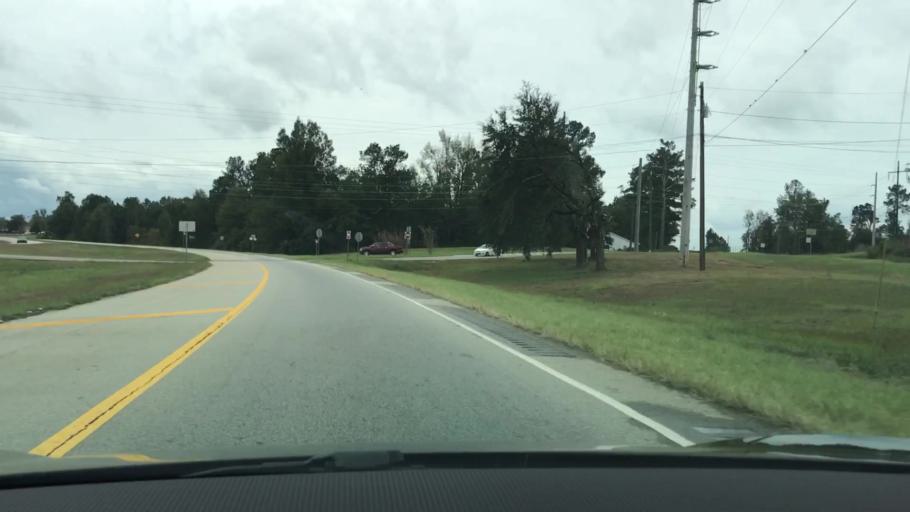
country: US
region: Georgia
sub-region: Jefferson County
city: Louisville
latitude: 33.0159
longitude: -82.4039
